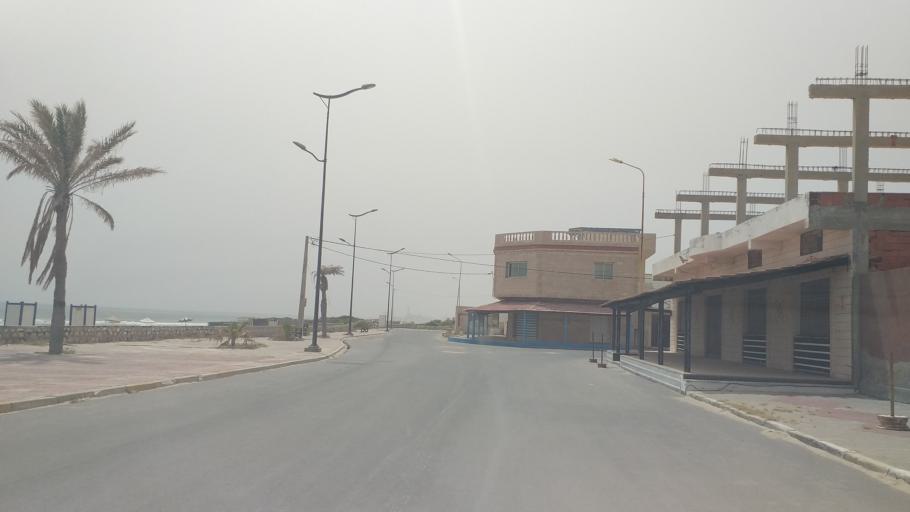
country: TN
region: Qabis
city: Gabes
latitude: 33.9532
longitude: 10.0711
